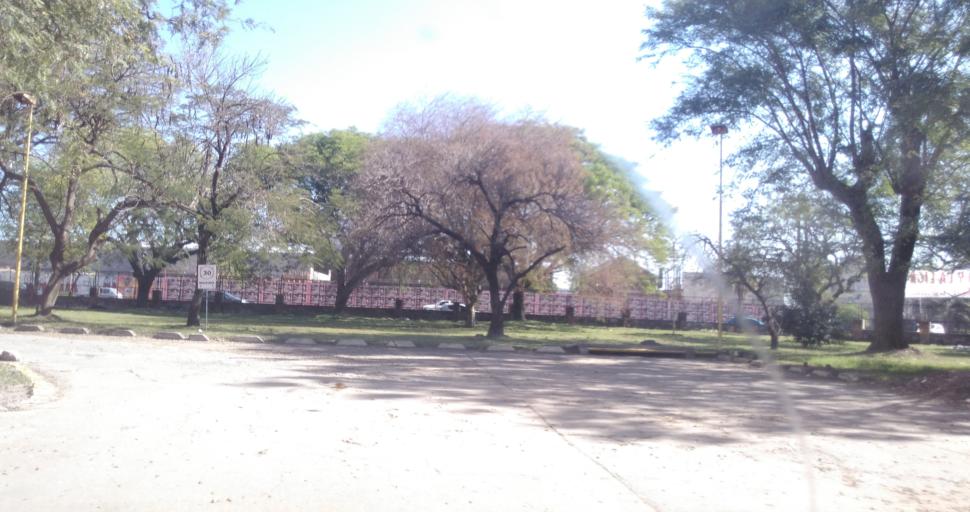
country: AR
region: Chaco
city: Resistencia
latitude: -27.4638
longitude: -58.9855
